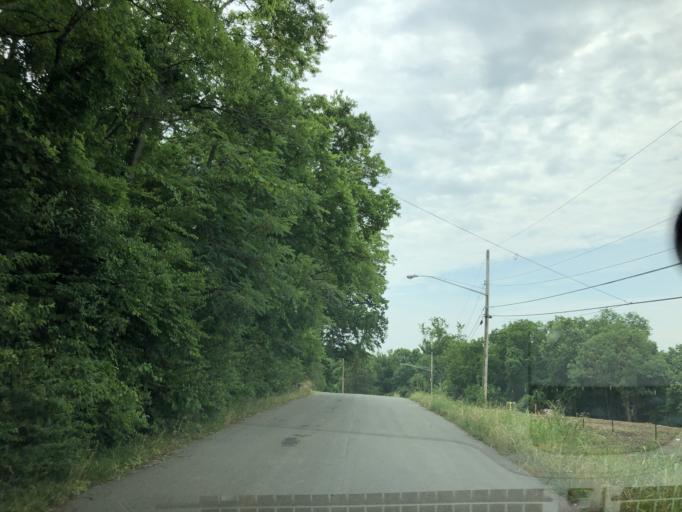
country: US
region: Tennessee
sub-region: Rutherford County
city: La Vergne
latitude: 36.0629
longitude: -86.6729
